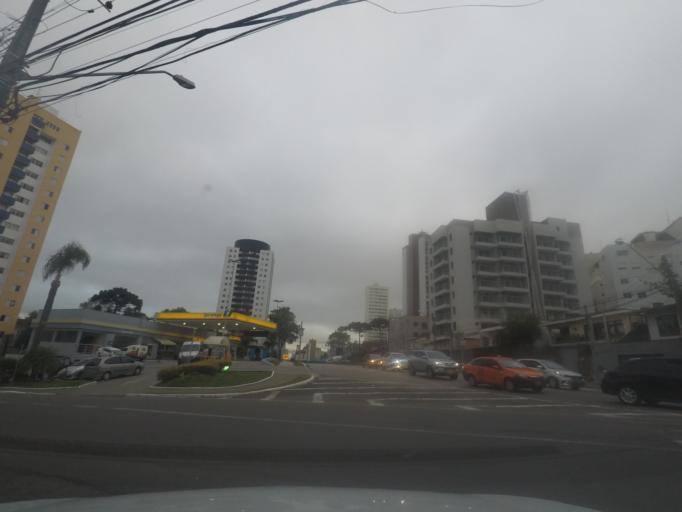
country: BR
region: Parana
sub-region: Curitiba
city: Curitiba
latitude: -25.4329
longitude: -49.2543
